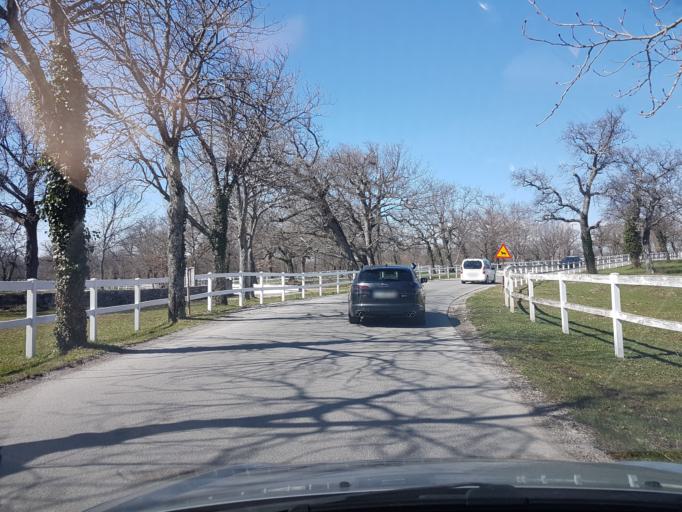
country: SI
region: Sezana
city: Sezana
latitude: 45.6662
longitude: 13.8878
